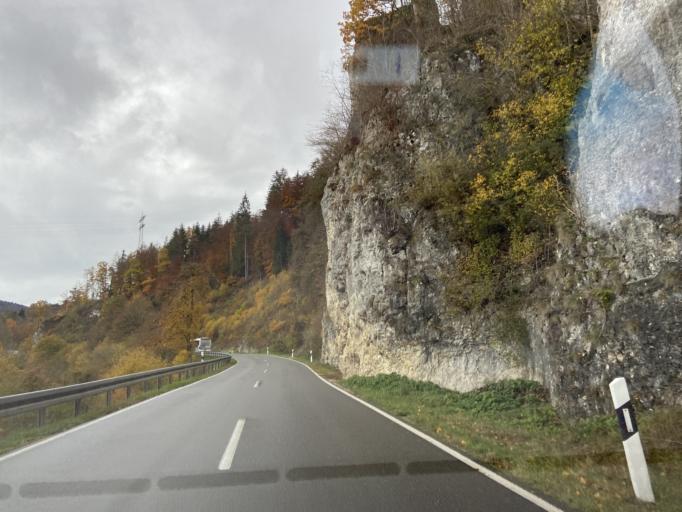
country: DE
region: Baden-Wuerttemberg
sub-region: Tuebingen Region
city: Stetten am Kalten Markt
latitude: 48.0937
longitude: 9.1016
